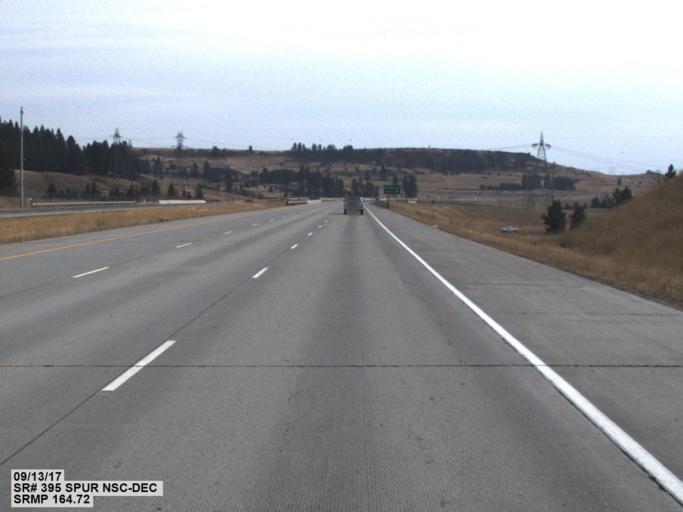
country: US
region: Washington
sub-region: Spokane County
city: Mead
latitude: 47.7592
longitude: -117.3652
